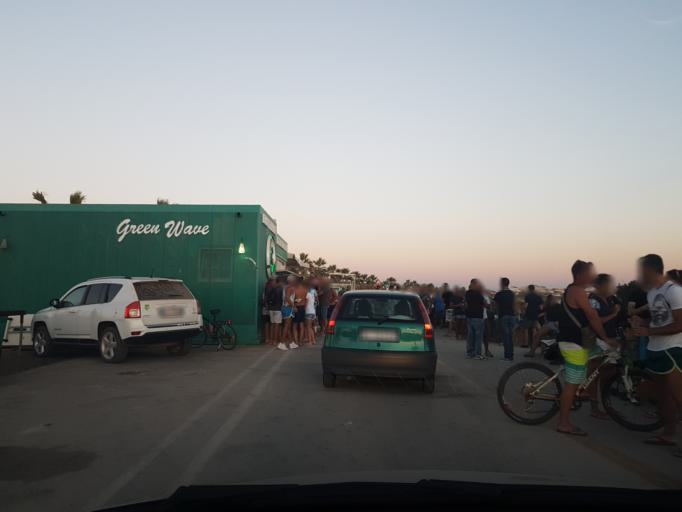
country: IT
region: Sardinia
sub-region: Provincia di Oristano
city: Riola Sardo
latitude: 40.0315
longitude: 8.4041
